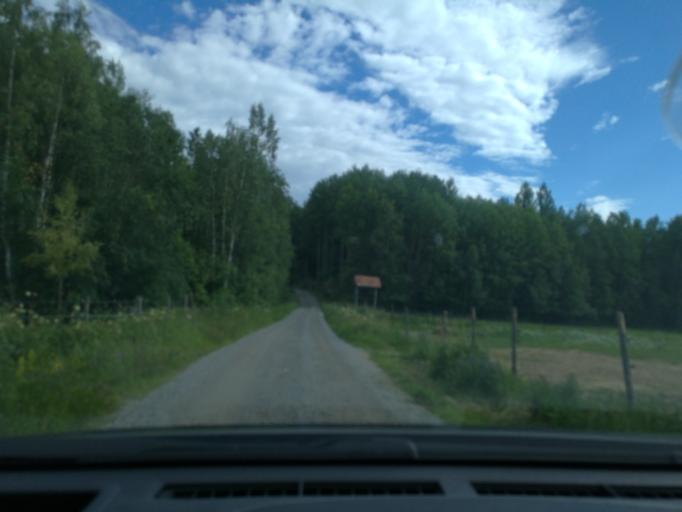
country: SE
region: Vaestmanland
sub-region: Surahammars Kommun
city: Ramnas
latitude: 59.7923
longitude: 16.3051
